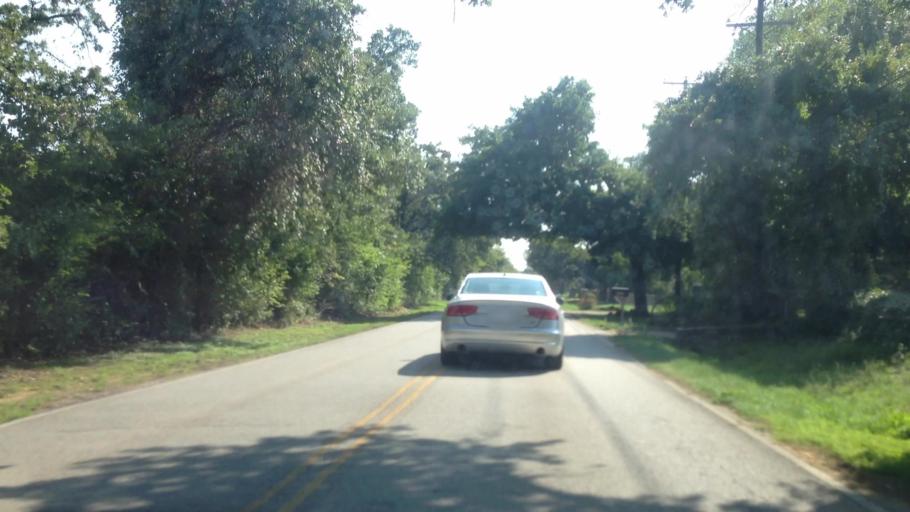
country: US
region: Texas
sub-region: Tarrant County
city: Colleyville
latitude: 32.8962
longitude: -97.1647
